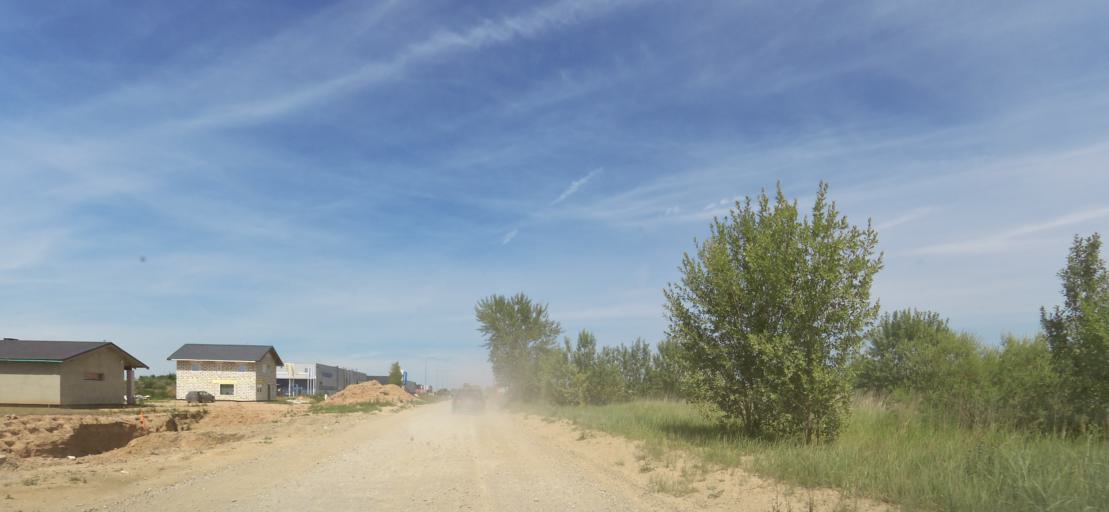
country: LT
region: Panevezys
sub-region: Panevezys City
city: Panevezys
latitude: 55.7250
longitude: 24.2975
